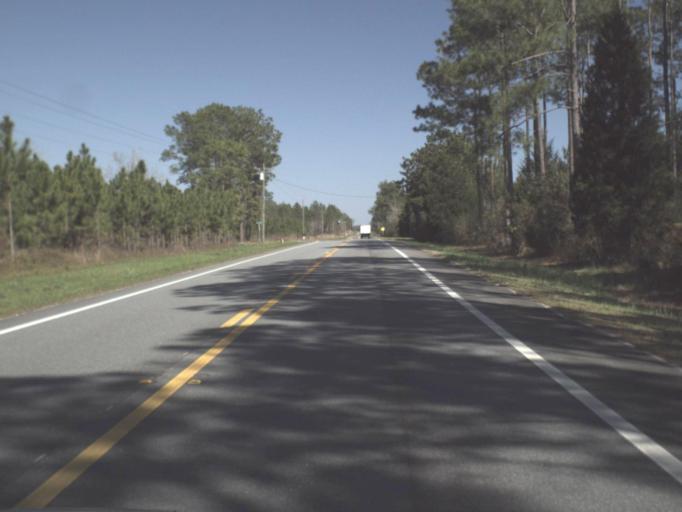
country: US
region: Florida
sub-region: Gulf County
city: Wewahitchka
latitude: 30.2598
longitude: -85.1925
